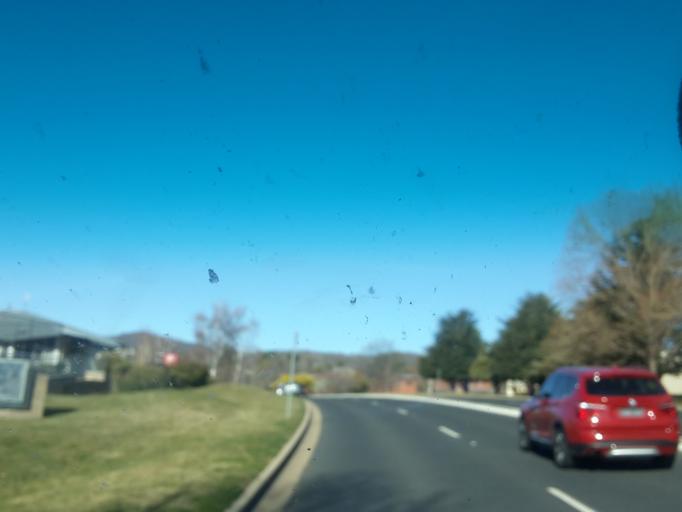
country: AU
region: New South Wales
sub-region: Snowy River
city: Jindabyne
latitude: -36.4151
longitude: 148.6156
